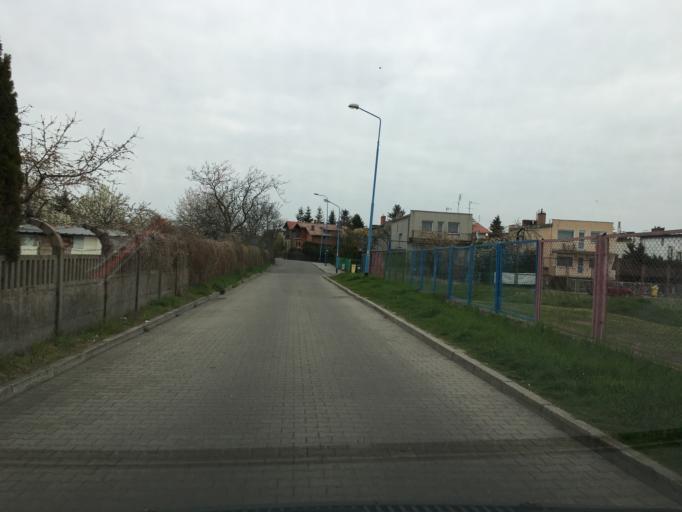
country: PL
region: Lower Silesian Voivodeship
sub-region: Legnica
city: Legnica
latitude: 51.1981
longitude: 16.1840
